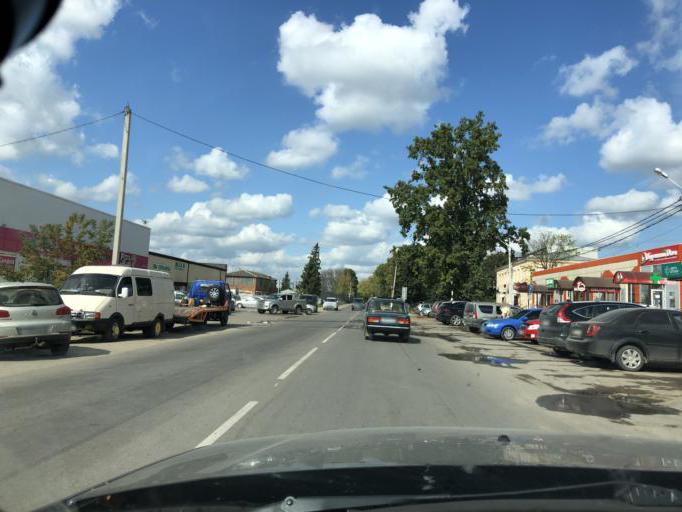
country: RU
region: Tula
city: Yasnogorsk
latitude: 54.4803
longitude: 37.6853
